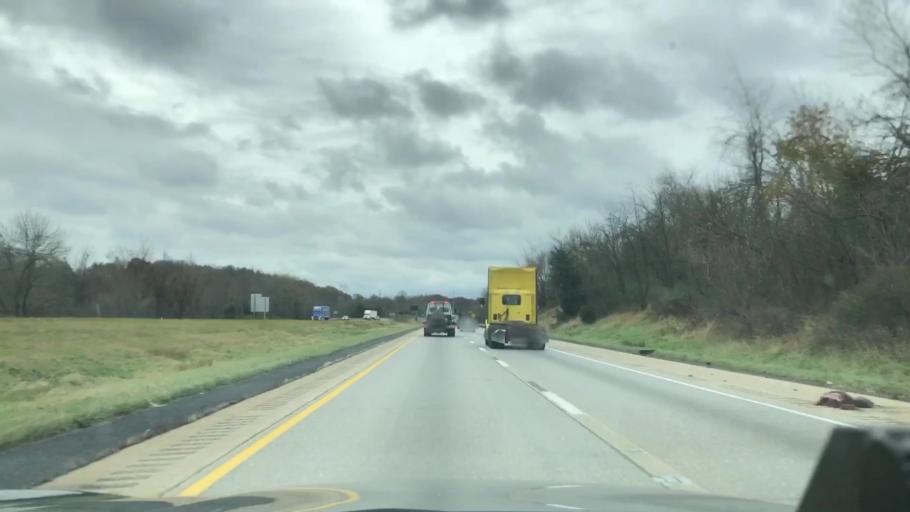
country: US
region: Pennsylvania
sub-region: Dauphin County
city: Skyline View
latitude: 40.3362
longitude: -76.7549
